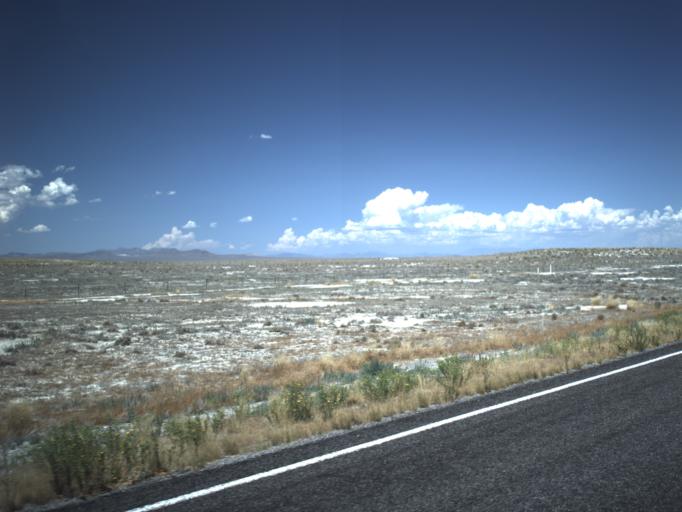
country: US
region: Utah
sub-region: Millard County
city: Delta
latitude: 39.1832
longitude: -113.0128
